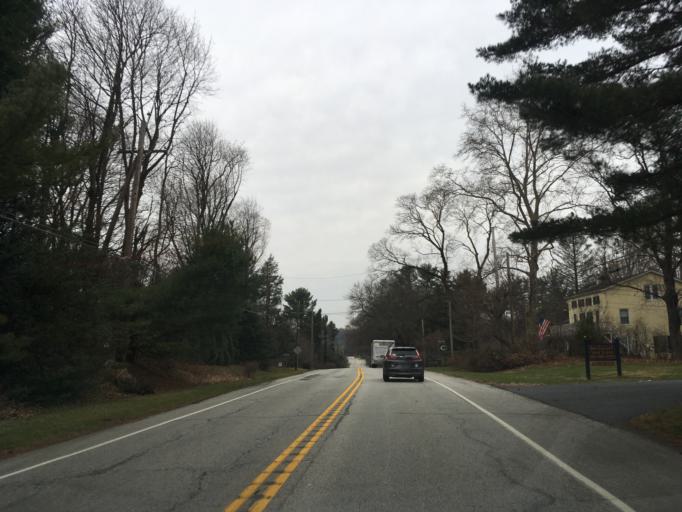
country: US
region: Delaware
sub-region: New Castle County
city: Greenville
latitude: 39.8452
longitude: -75.6318
